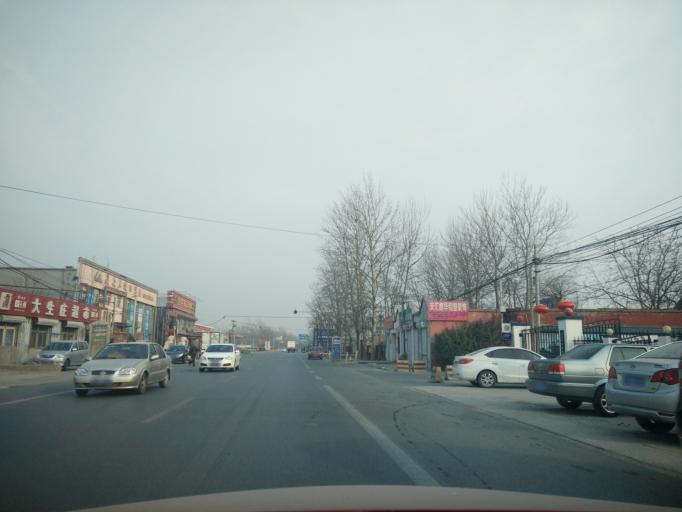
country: CN
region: Beijing
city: Yinghai
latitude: 39.7650
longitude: 116.4019
